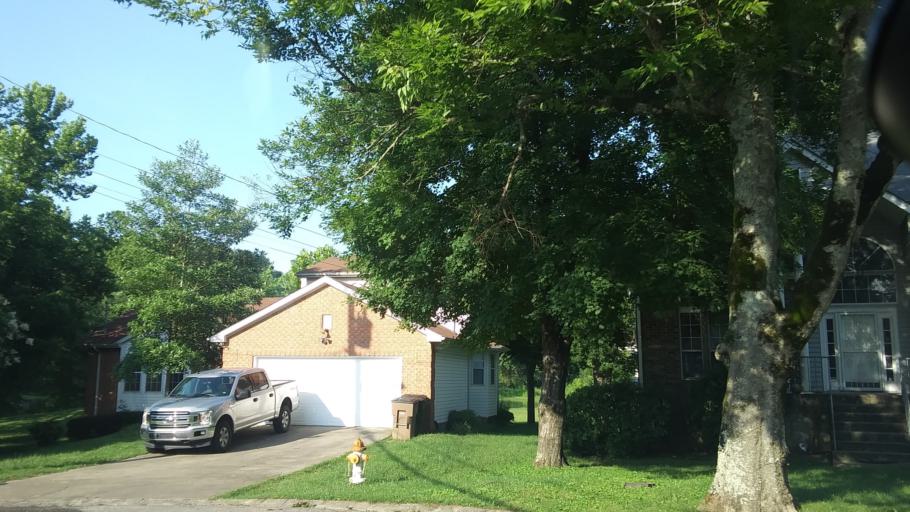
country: US
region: Tennessee
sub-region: Rutherford County
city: La Vergne
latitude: 36.0777
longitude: -86.6644
